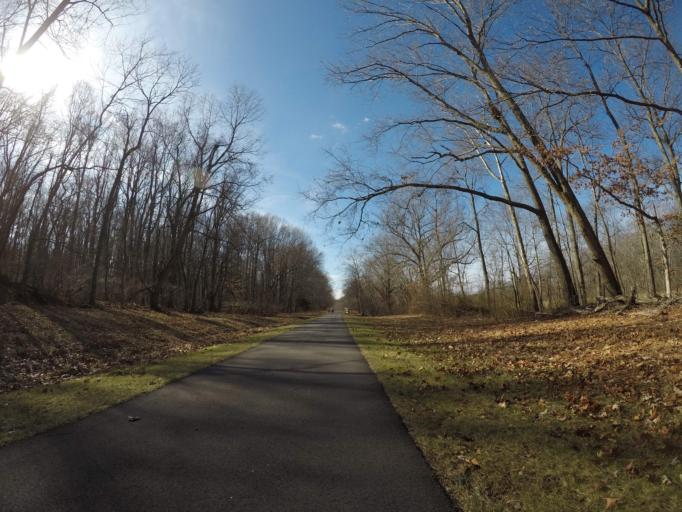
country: US
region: Maryland
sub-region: Charles County
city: Bennsville
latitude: 38.5962
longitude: -77.0376
